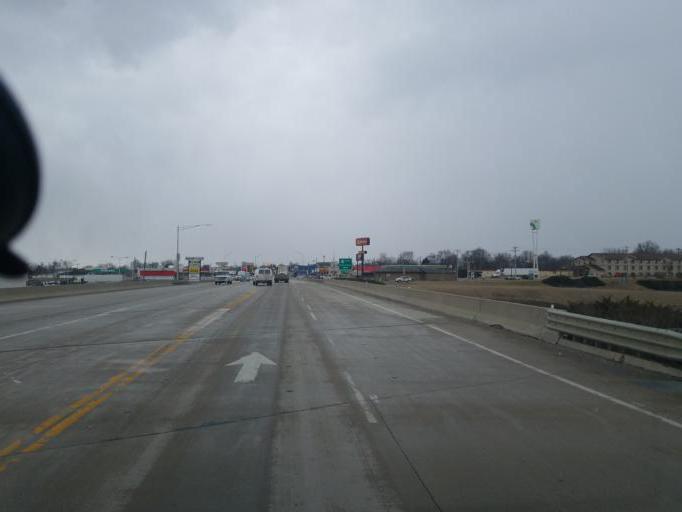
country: US
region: Missouri
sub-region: Macon County
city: Macon
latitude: 39.7547
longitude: -92.4678
